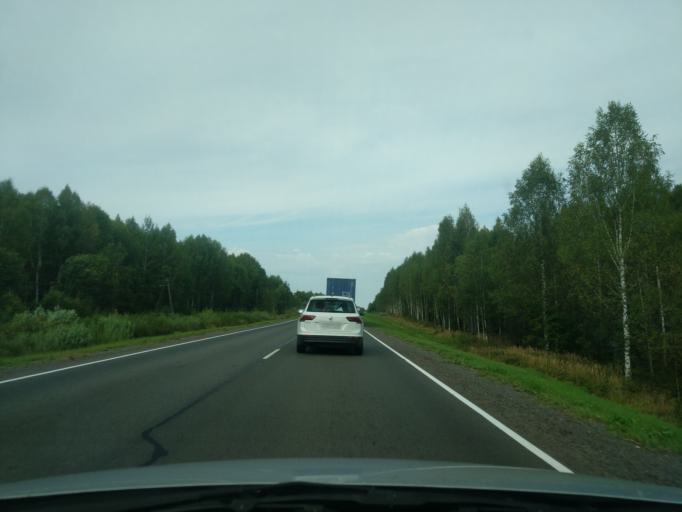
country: RU
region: Kirov
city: Leninskoye
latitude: 58.2847
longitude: 47.2552
